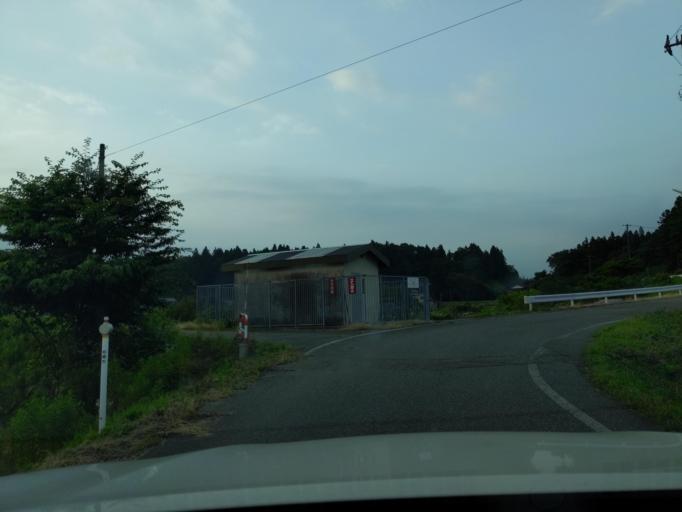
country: JP
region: Niigata
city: Kashiwazaki
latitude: 37.4389
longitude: 138.6522
